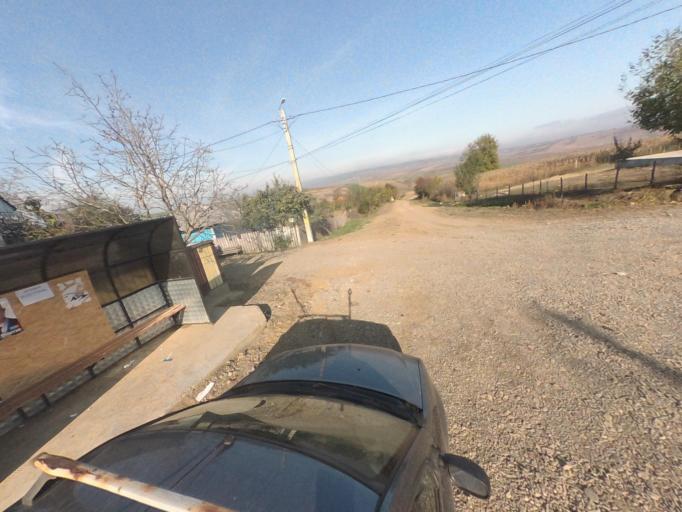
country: RO
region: Vaslui
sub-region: Comuna Bacesti
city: Bacesti
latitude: 46.8706
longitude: 27.2046
